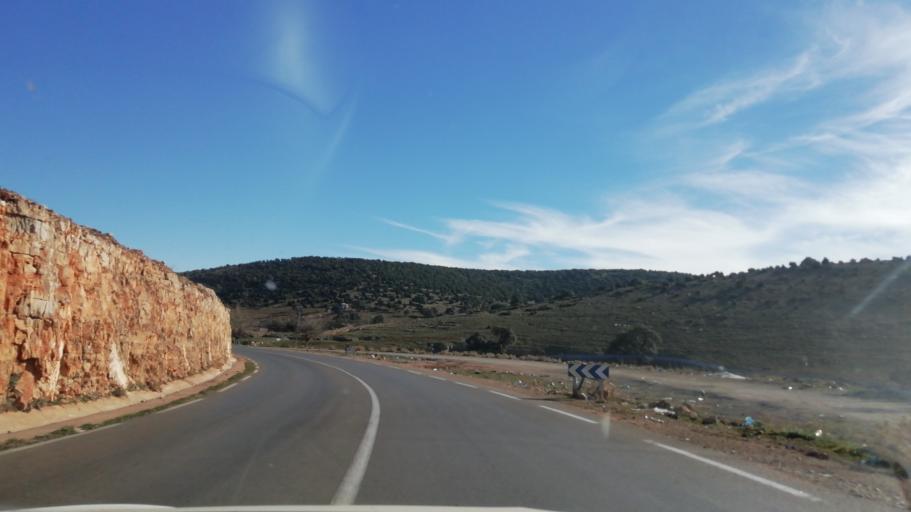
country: DZ
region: Tlemcen
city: Sebdou
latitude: 34.7170
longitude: -1.3363
